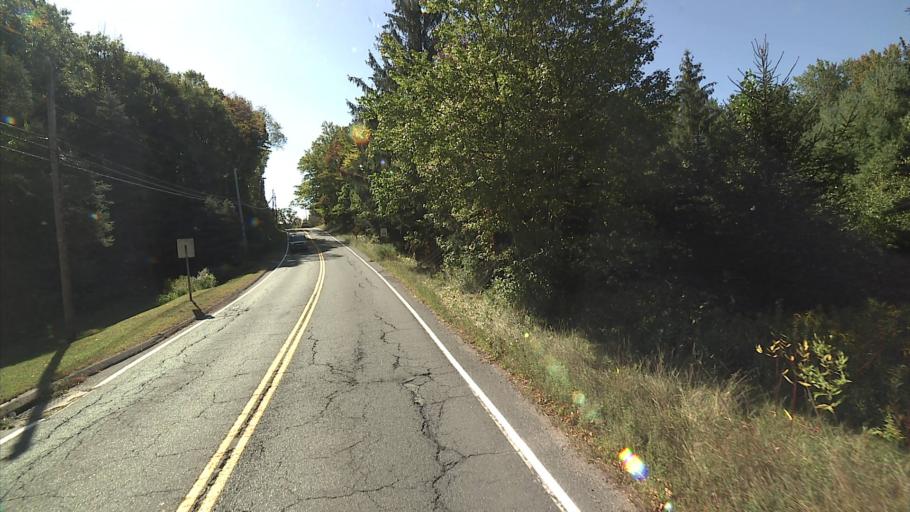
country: US
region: Connecticut
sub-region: Hartford County
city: Bristol
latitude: 41.7170
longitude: -72.9480
